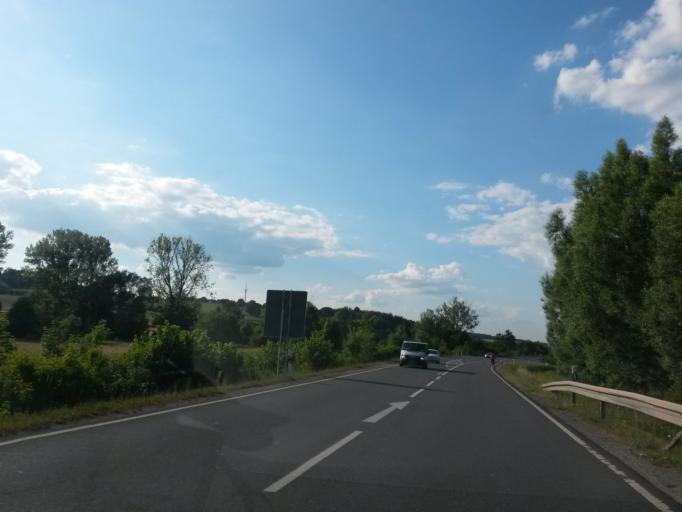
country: DE
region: Bavaria
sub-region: Regierungsbezirk Mittelfranken
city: Diespeck
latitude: 49.5923
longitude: 10.6232
